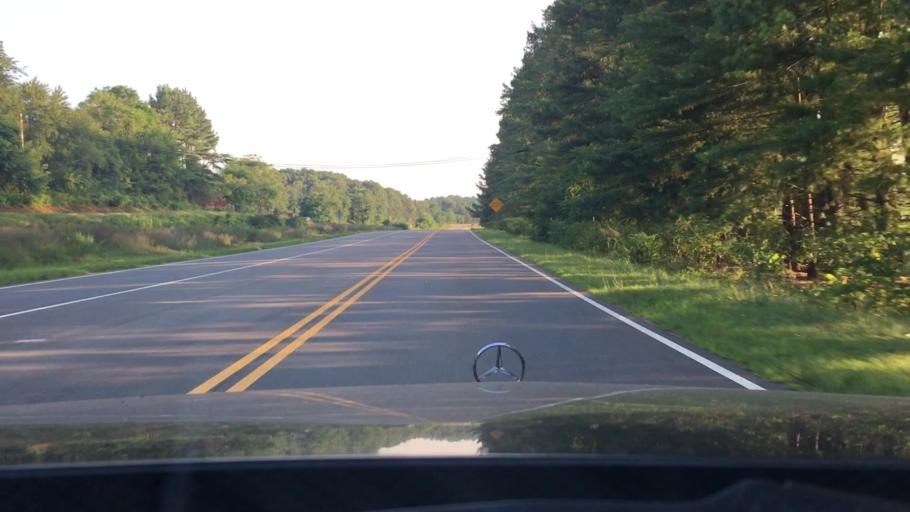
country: US
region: Virginia
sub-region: Pittsylvania County
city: Hurt
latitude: 37.0989
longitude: -79.3048
